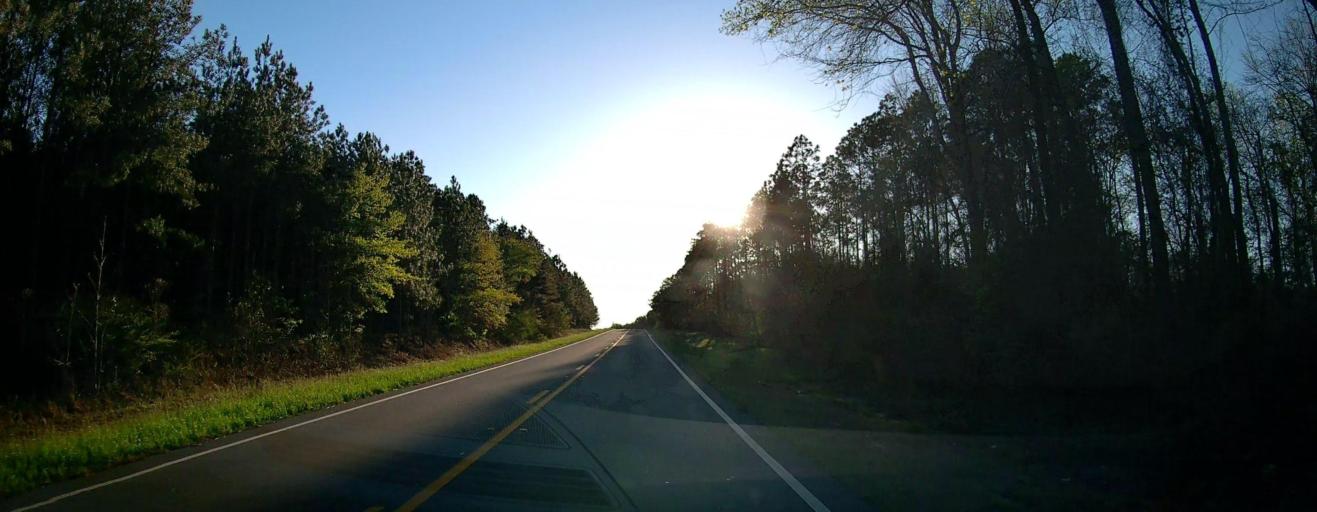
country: US
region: Georgia
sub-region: Wilcox County
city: Abbeville
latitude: 31.9865
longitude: -83.3380
